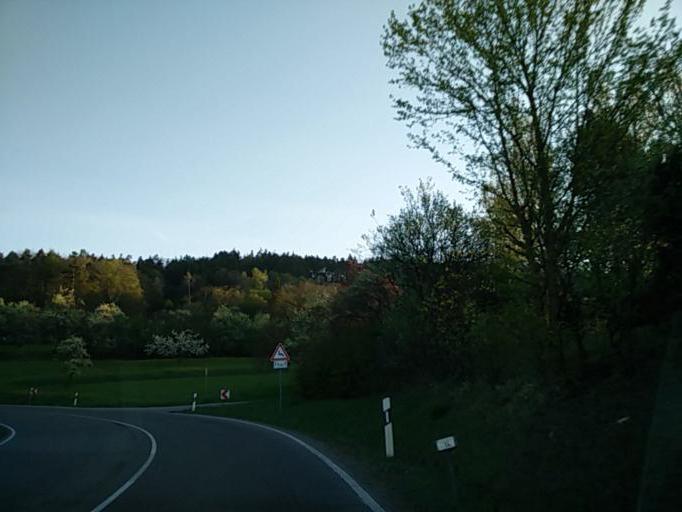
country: DE
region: Baden-Wuerttemberg
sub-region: Regierungsbezirk Stuttgart
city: Nufringen
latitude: 48.6005
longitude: 8.8890
